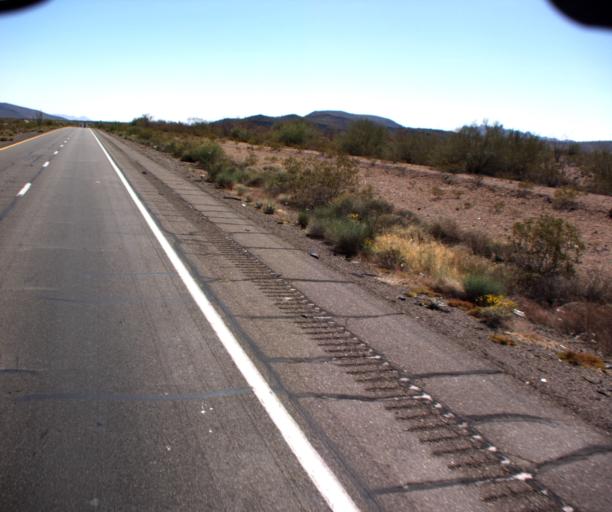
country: US
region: Arizona
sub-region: La Paz County
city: Quartzsite
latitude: 33.6573
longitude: -113.9762
